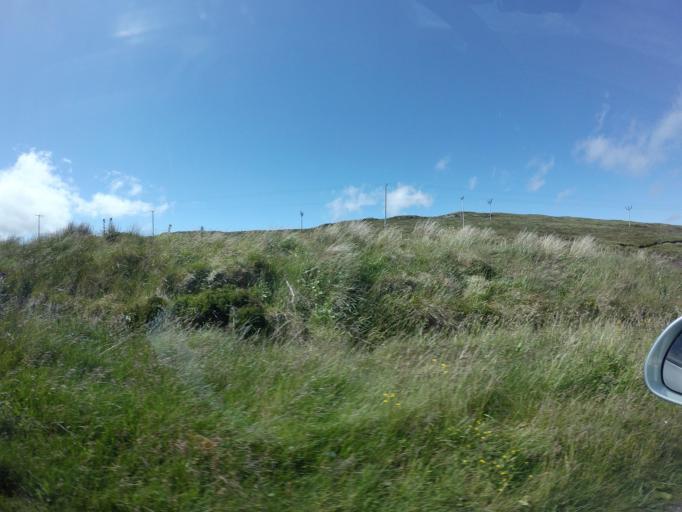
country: GB
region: Scotland
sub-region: Eilean Siar
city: Stornoway
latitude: 58.1279
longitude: -6.5067
